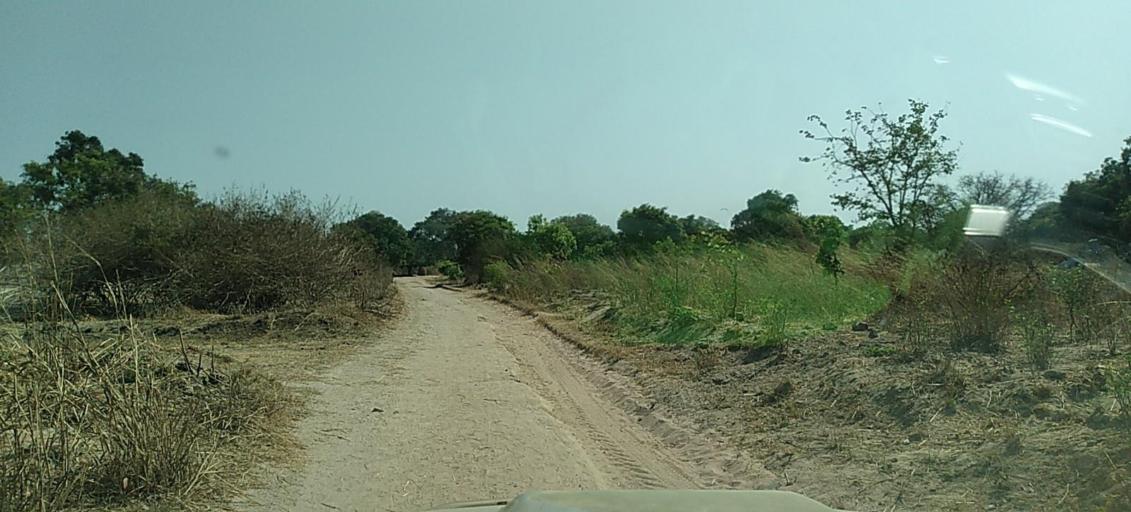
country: ZM
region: North-Western
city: Kalengwa
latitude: -13.3587
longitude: 24.8628
